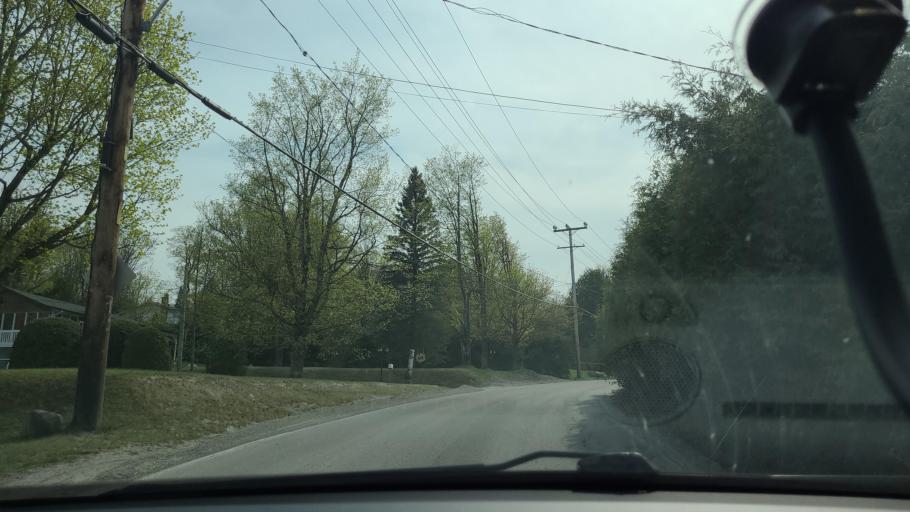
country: CA
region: Quebec
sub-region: Laurentides
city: Prevost
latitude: 45.8930
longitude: -74.0415
